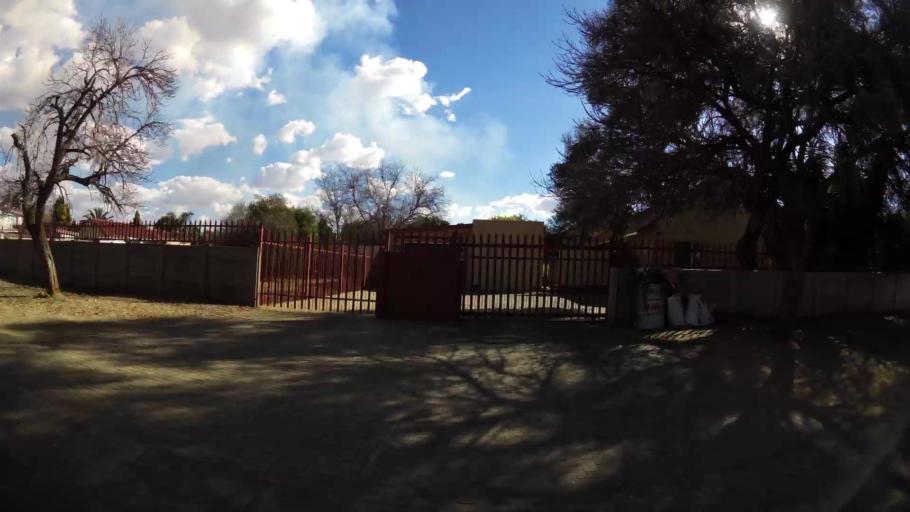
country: ZA
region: North-West
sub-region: Dr Kenneth Kaunda District Municipality
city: Klerksdorp
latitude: -26.8299
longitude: 26.6569
